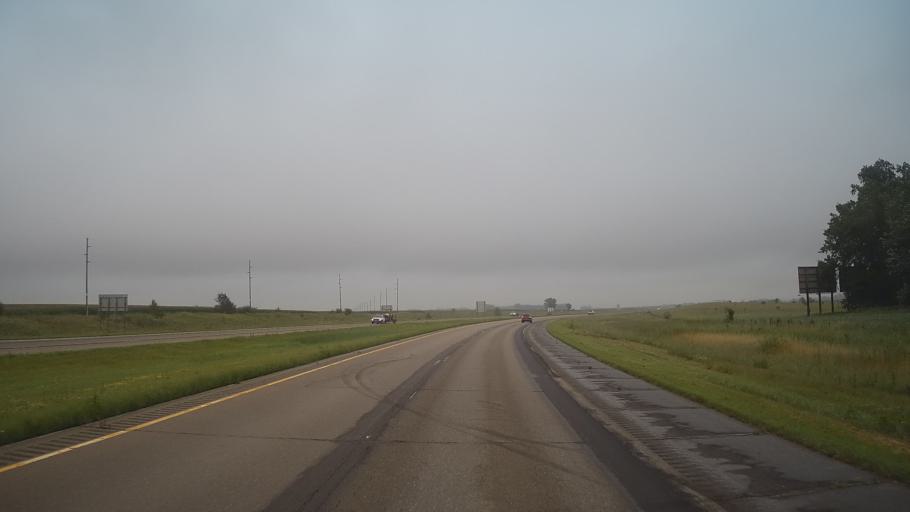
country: US
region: Minnesota
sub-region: Faribault County
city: Blue Earth
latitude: 43.6598
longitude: -94.0871
